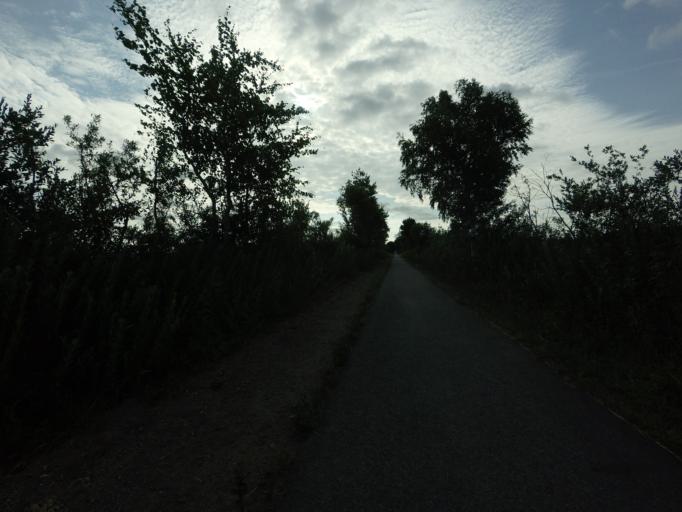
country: SE
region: Skane
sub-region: Hoganas Kommun
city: Hoganas
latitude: 56.1824
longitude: 12.6528
